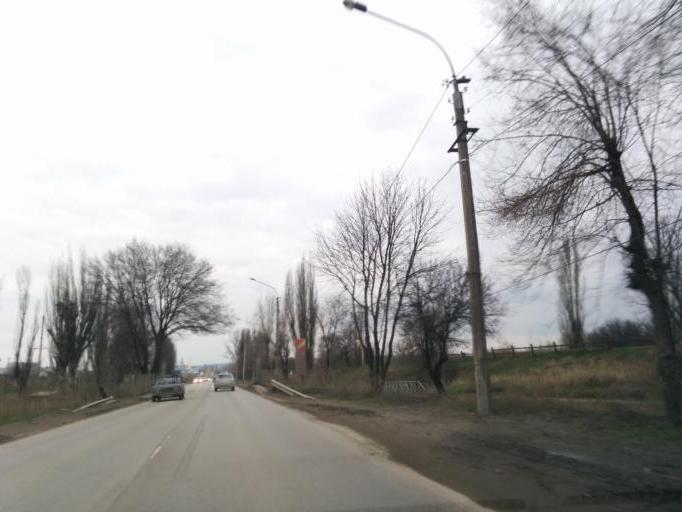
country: RU
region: Rostov
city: Novocherkassk
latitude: 47.4625
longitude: 40.1002
